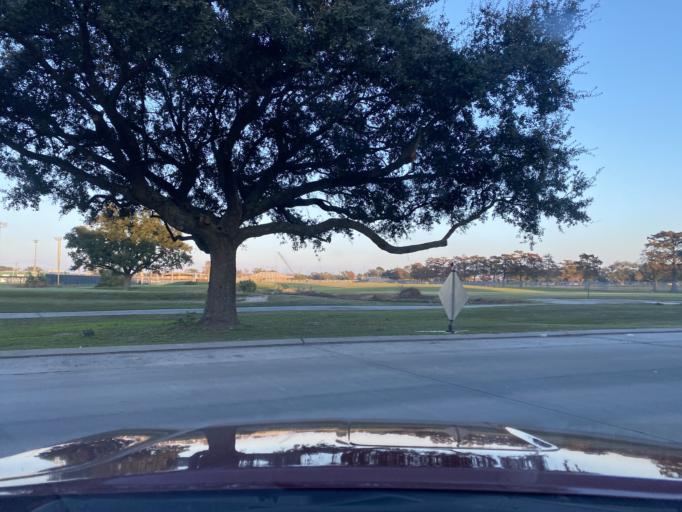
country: US
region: Louisiana
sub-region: Orleans Parish
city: New Orleans
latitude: 30.0266
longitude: -90.0435
